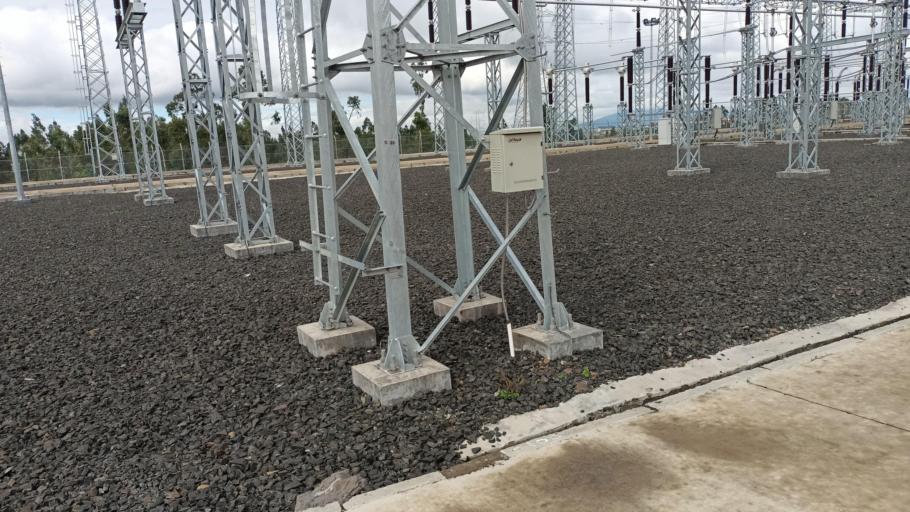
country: ET
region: Adis Abeba
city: Addis Ababa
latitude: 8.9678
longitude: 38.8682
